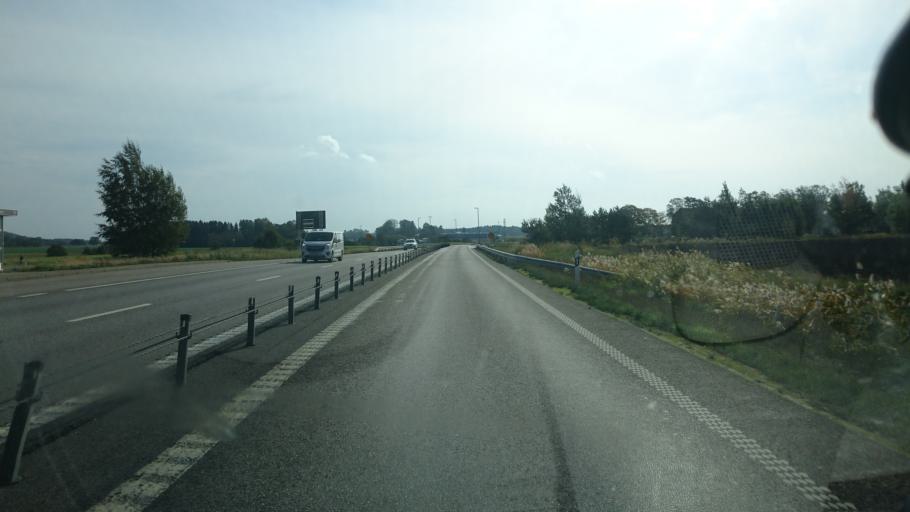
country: SE
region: Vaestra Goetaland
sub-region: Vanersborgs Kommun
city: Vargon
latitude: 58.2922
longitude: 12.3904
